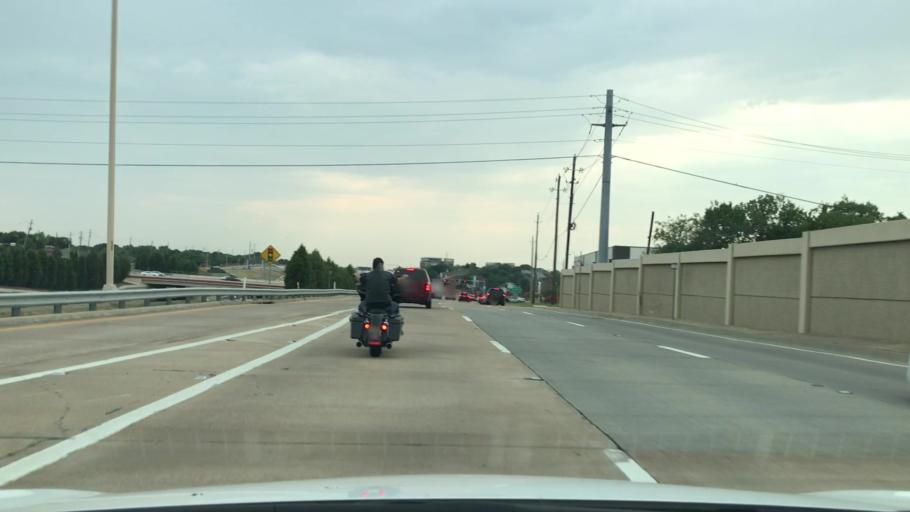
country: US
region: Texas
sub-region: Dallas County
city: Carrollton
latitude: 32.9861
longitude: -96.8877
